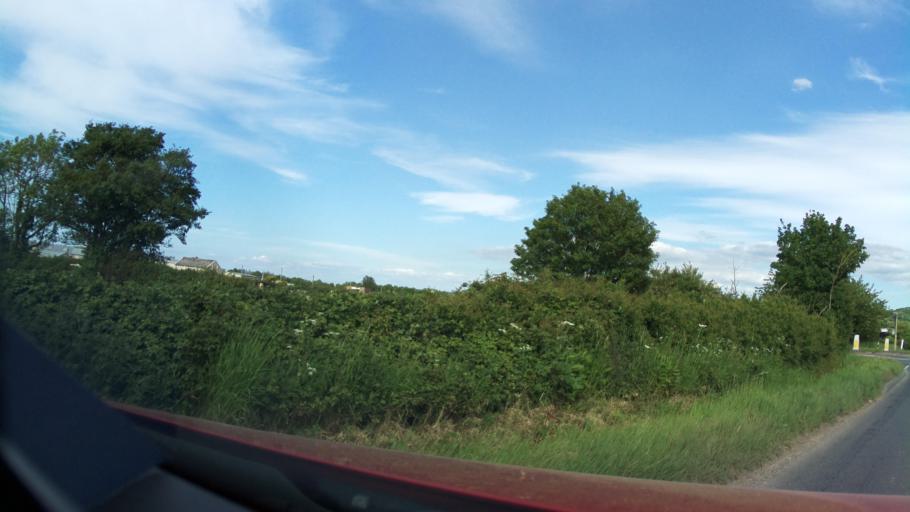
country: GB
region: England
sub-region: Worcestershire
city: Broadway
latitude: 52.0713
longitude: -1.8249
